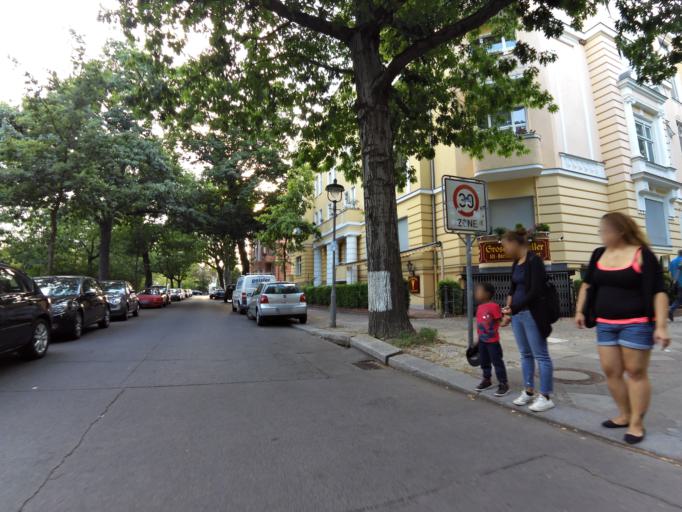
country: DE
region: Berlin
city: Steglitz Bezirk
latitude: 52.4620
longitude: 13.3392
